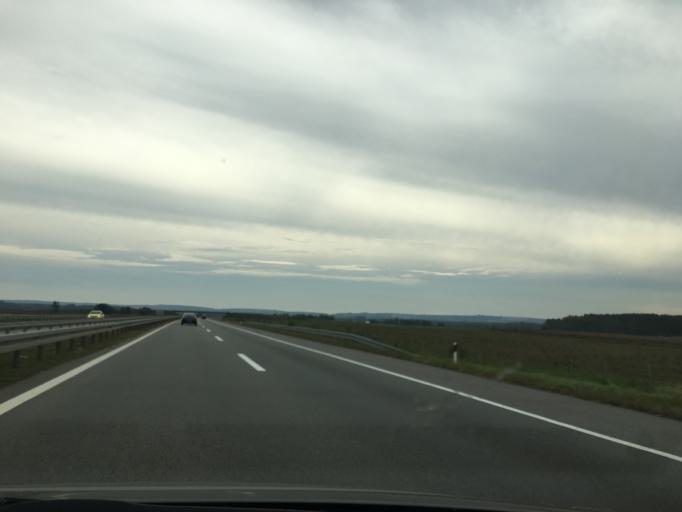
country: RS
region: Autonomna Pokrajina Vojvodina
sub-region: Juznobacki Okrug
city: Kovilj
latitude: 45.2138
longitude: 20.0655
